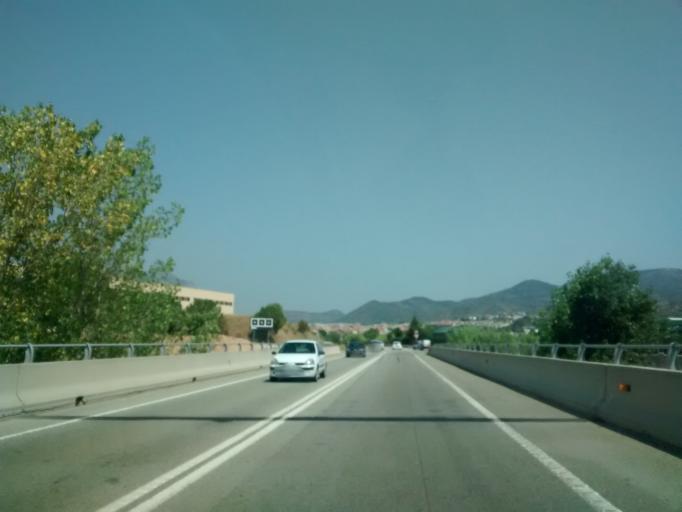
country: ES
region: Catalonia
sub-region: Provincia de Barcelona
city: Abrera
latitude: 41.5292
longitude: 1.9053
